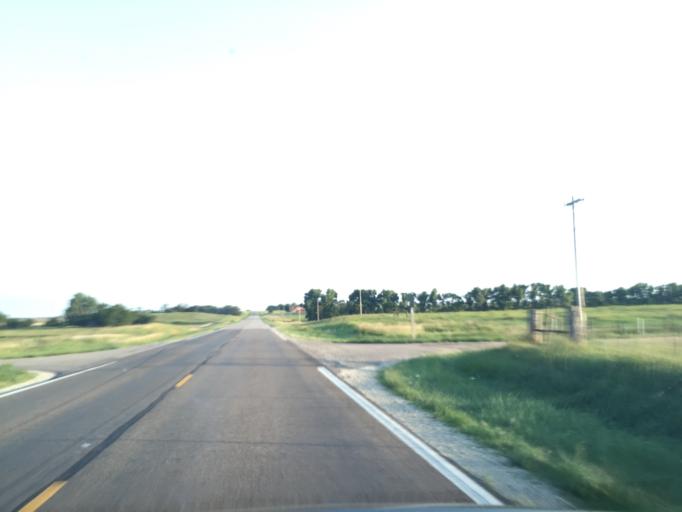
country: US
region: Kansas
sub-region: Ellsworth County
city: Ellsworth
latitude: 38.7696
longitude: -98.2250
